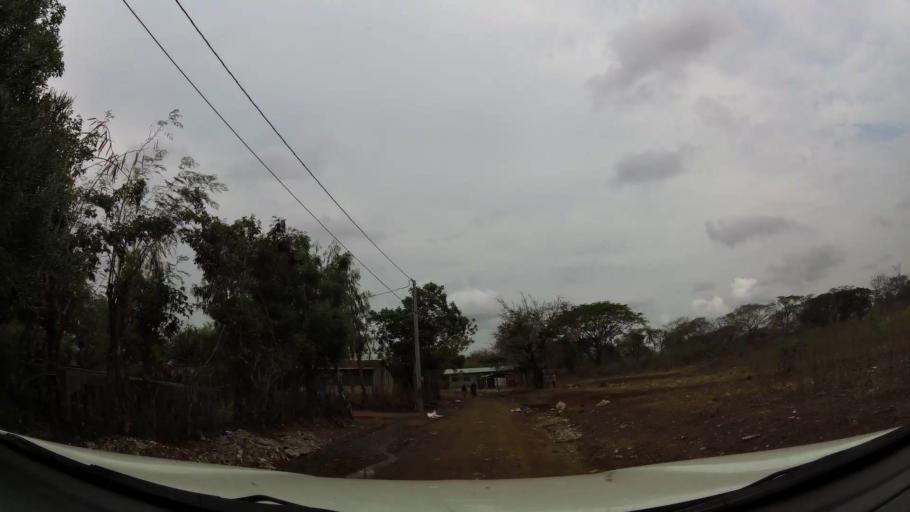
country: NI
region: Granada
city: Granada
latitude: 11.9118
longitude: -85.9610
